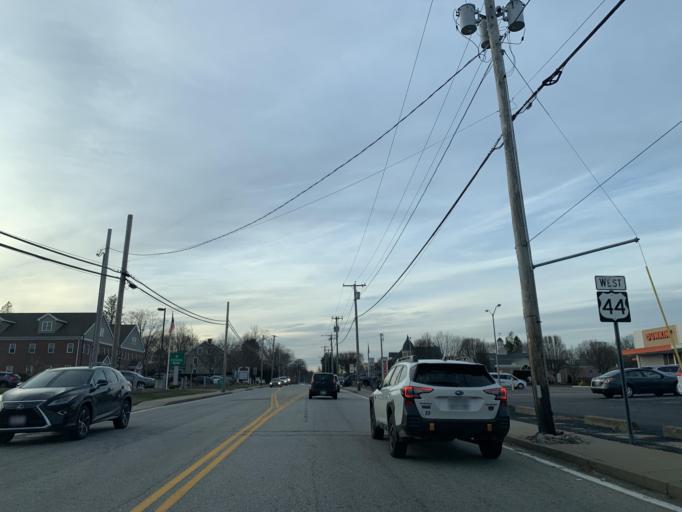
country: US
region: Rhode Island
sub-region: Providence County
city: Greenville
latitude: 41.8727
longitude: -71.5548
